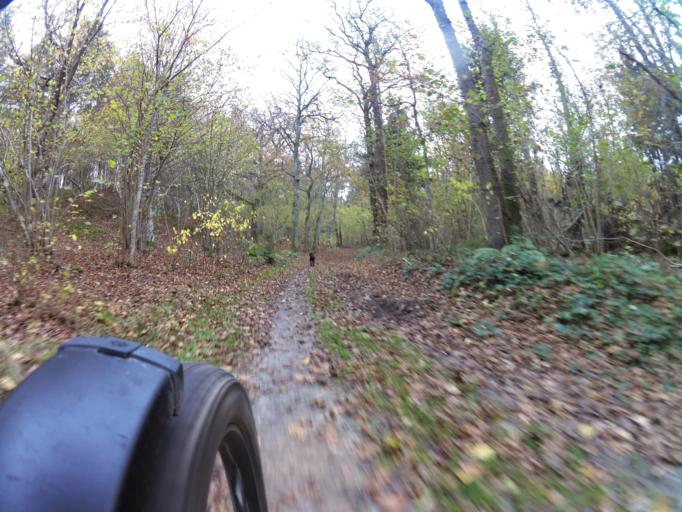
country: PL
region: Pomeranian Voivodeship
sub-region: Powiat pucki
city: Krokowa
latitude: 54.8308
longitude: 18.1148
